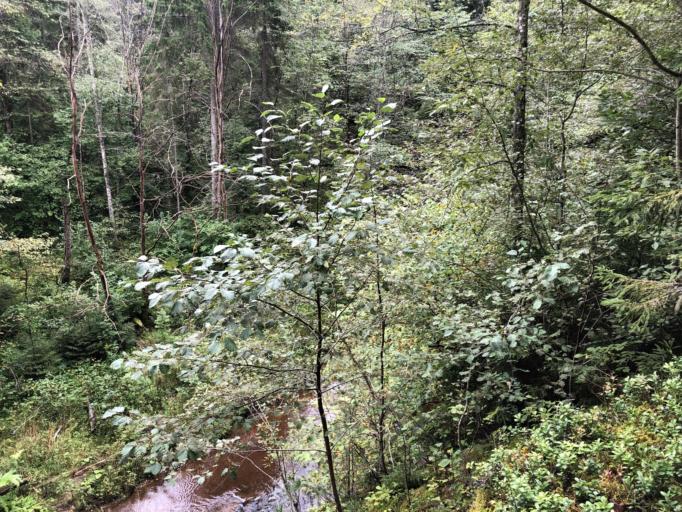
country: LV
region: Priekuli
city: Priekuli
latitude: 57.3223
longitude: 25.4222
